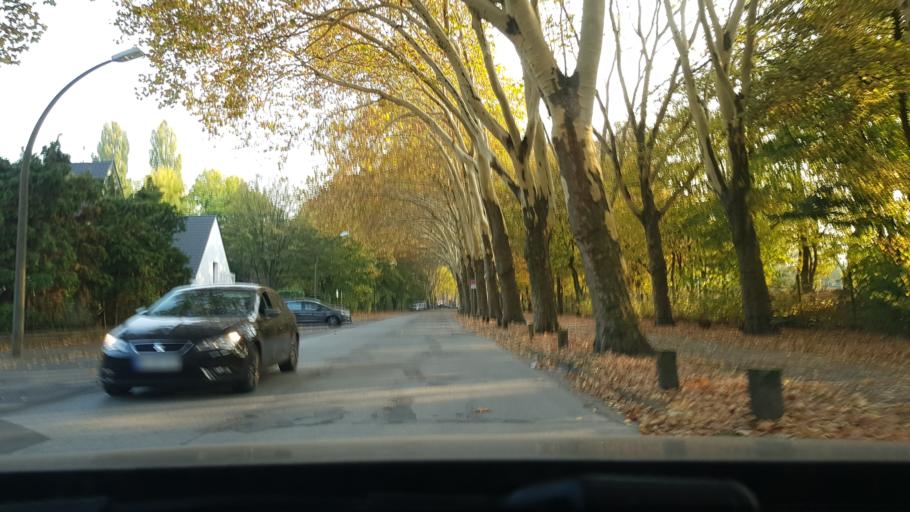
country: DE
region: North Rhine-Westphalia
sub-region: Regierungsbezirk Dusseldorf
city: Hochfeld
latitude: 51.4089
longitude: 6.7074
